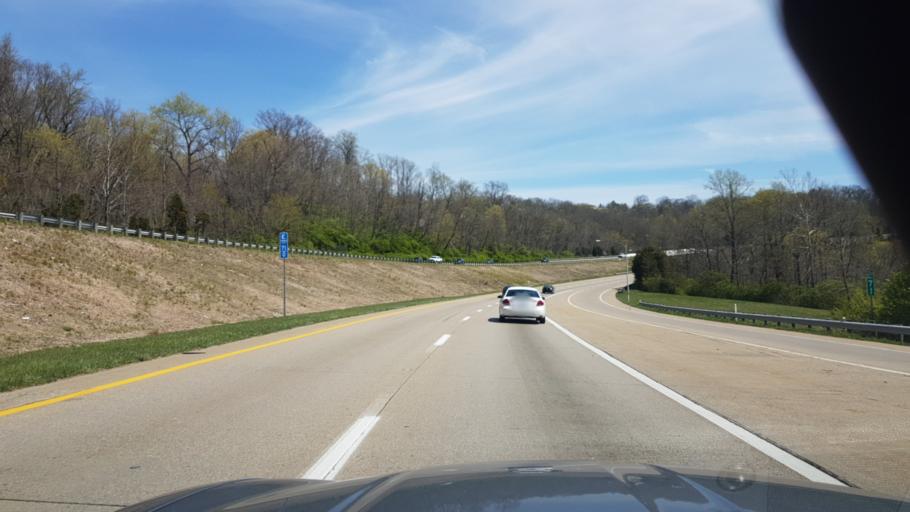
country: US
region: Ohio
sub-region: Hamilton County
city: Salem Heights
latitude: 39.0563
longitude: -84.3889
